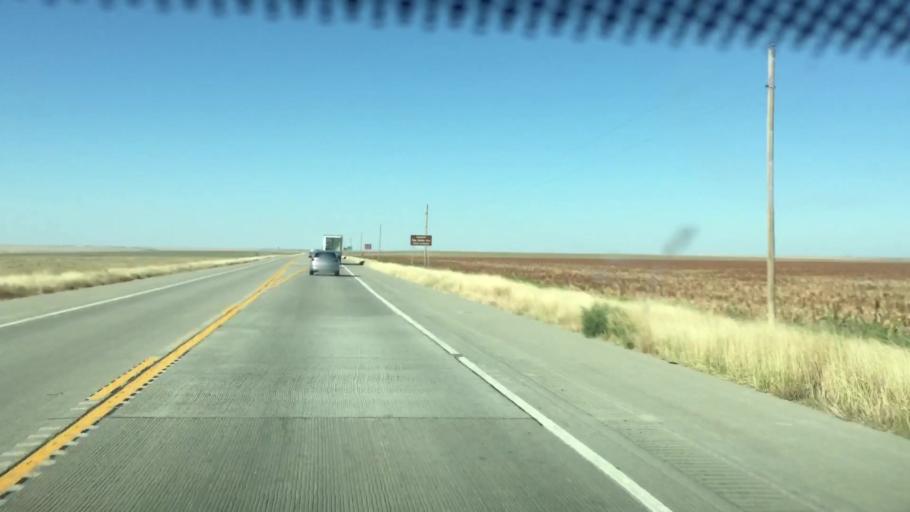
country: US
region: Colorado
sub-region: Kiowa County
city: Eads
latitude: 38.2919
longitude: -102.7199
